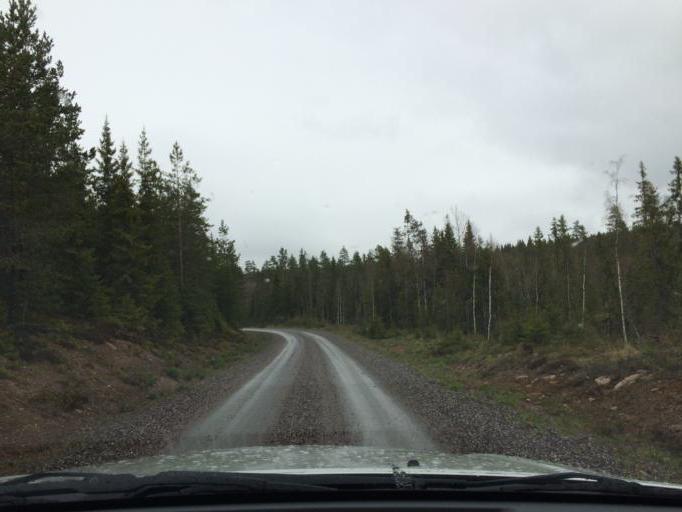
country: SE
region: Dalarna
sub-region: Ludvika Kommun
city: Abborrberget
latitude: 60.0302
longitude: 14.6411
